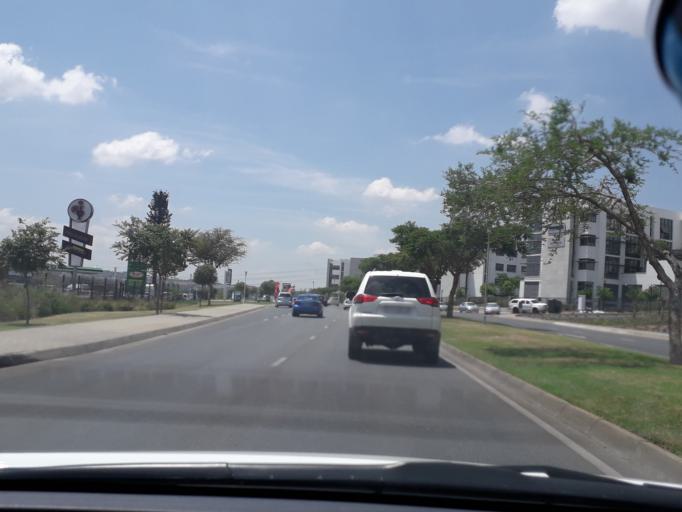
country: ZA
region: Gauteng
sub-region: City of Johannesburg Metropolitan Municipality
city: Midrand
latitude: -26.0126
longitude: 28.1009
